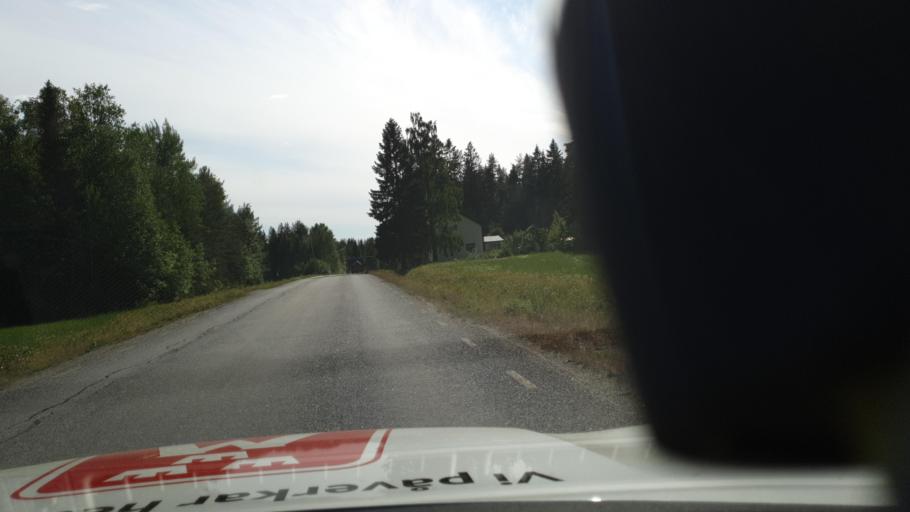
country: SE
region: Vaesterbotten
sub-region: Skelleftea Kommun
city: Burtraesk
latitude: 64.6089
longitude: 20.5883
